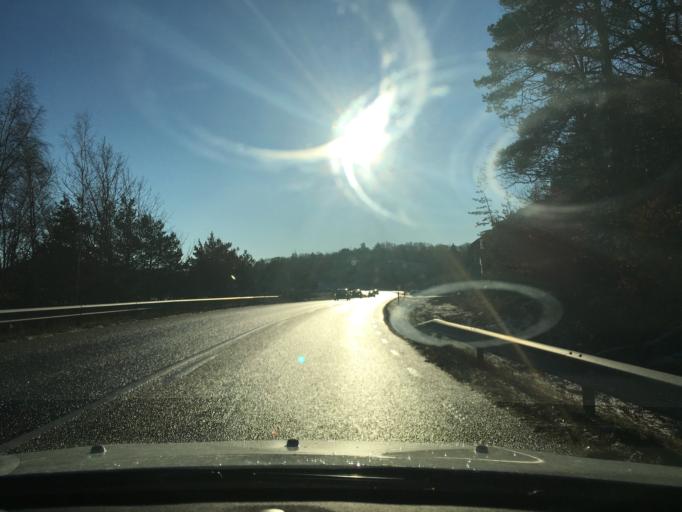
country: SE
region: Vaestra Goetaland
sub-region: Tjorns Kommun
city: Myggenas
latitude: 58.0734
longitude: 11.6965
